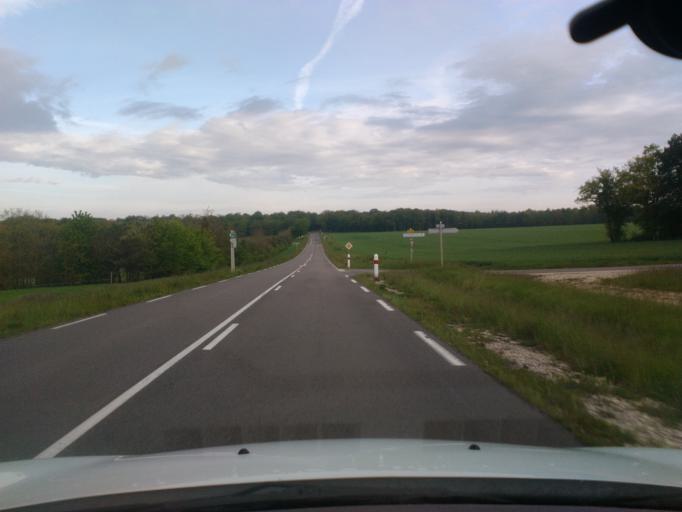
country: FR
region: Champagne-Ardenne
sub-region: Departement de la Haute-Marne
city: Lavilleneuve-au-Roi
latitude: 48.2024
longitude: 4.9393
